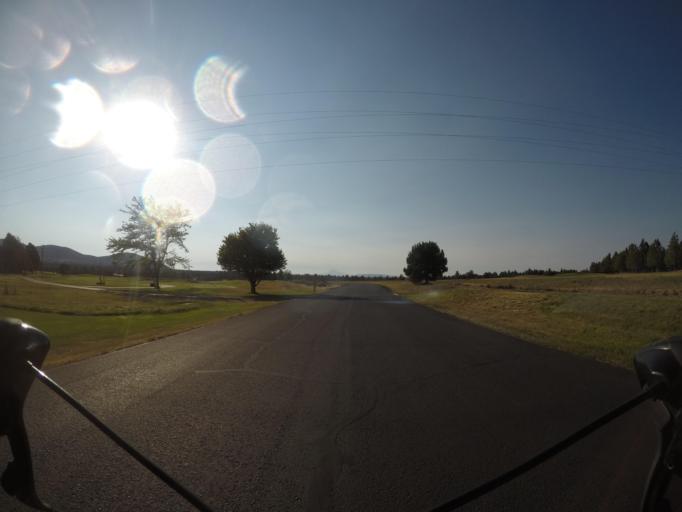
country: US
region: Oregon
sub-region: Deschutes County
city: Redmond
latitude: 44.2610
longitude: -121.2513
